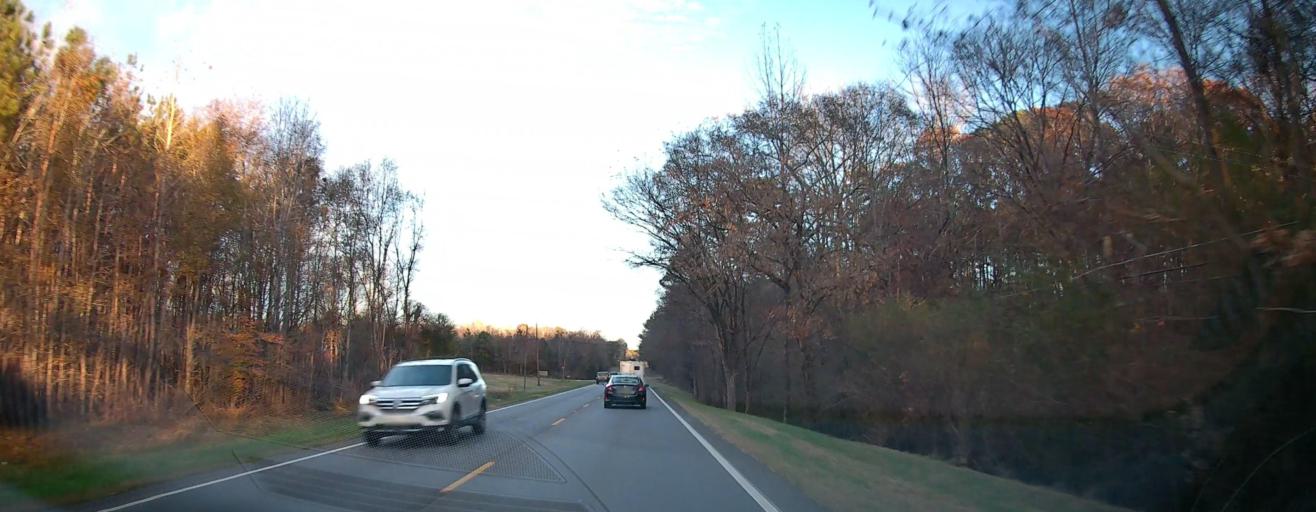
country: US
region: Alabama
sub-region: Etowah County
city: Attalla
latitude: 34.0401
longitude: -86.1333
